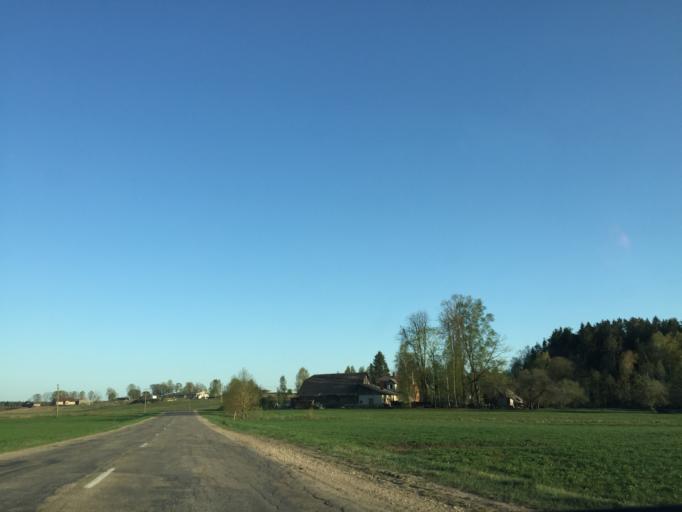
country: LV
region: Koknese
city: Koknese
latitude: 56.7148
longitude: 25.4909
